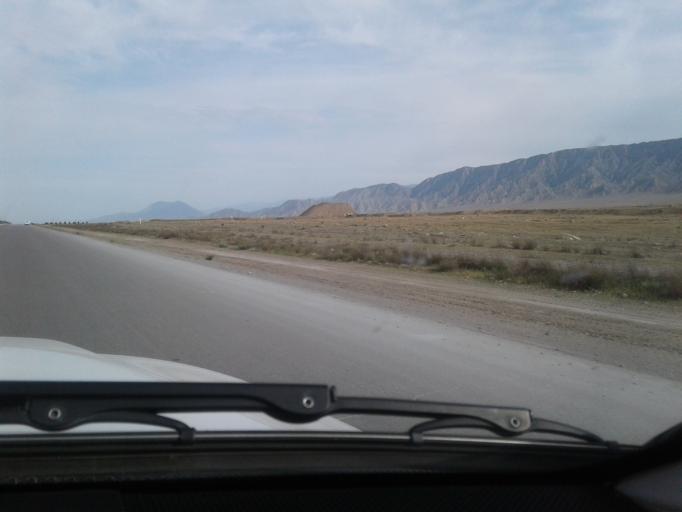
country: TM
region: Ahal
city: Baharly
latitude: 38.2243
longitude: 57.7961
